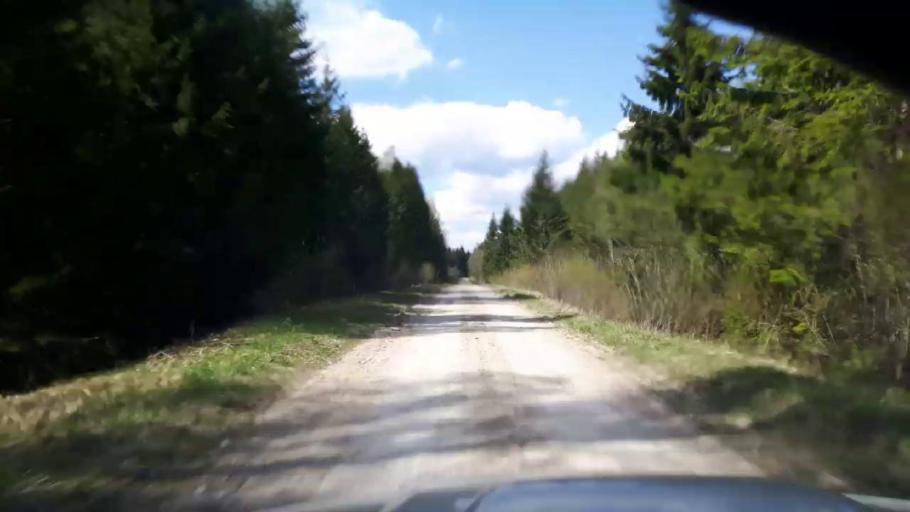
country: EE
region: Paernumaa
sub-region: Tootsi vald
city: Tootsi
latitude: 58.4455
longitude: 24.9097
